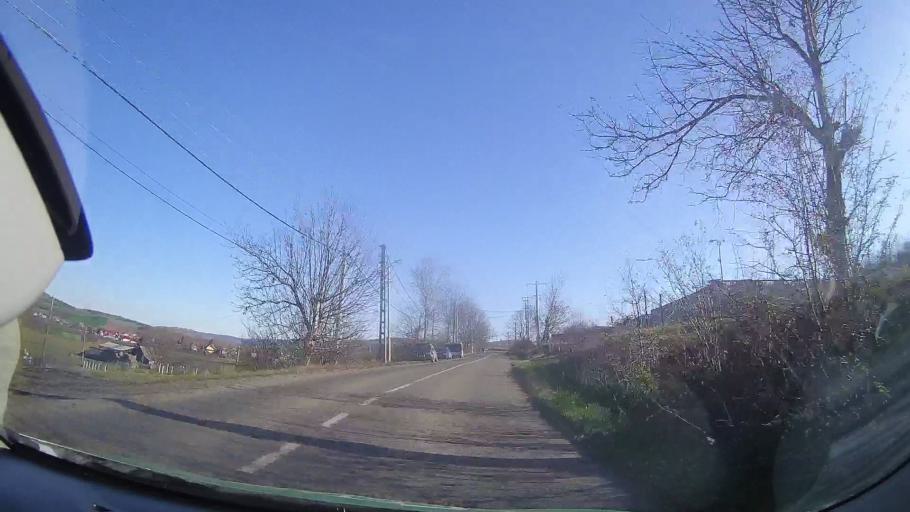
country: RO
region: Mures
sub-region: Comuna Band
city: Band
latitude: 46.5815
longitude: 24.3559
